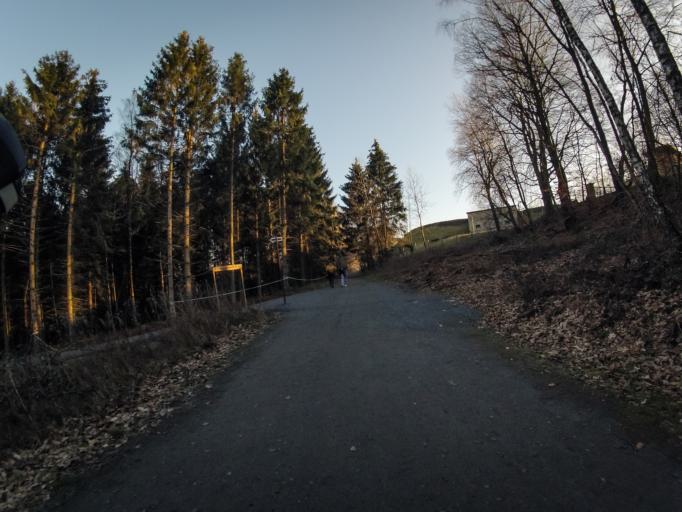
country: DE
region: Lower Saxony
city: Wallenhorst
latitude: 52.3212
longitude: 8.0269
